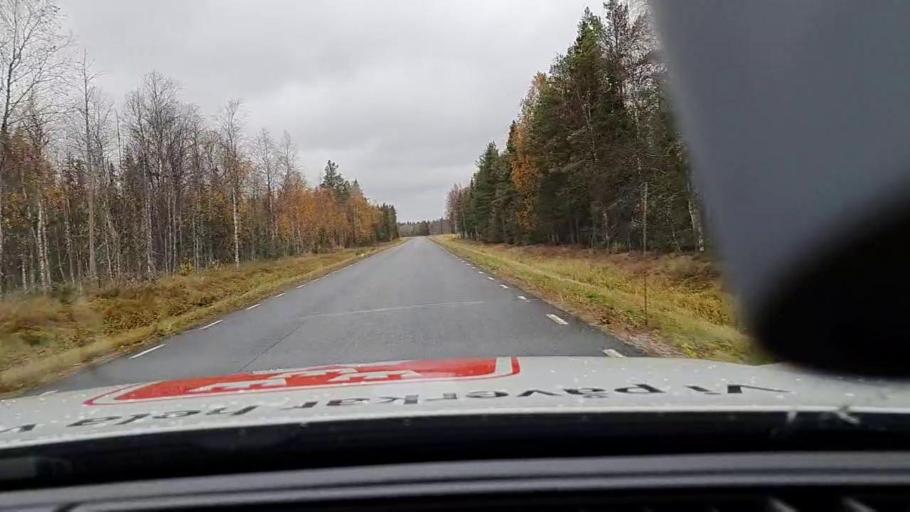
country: SE
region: Norrbotten
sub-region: Haparanda Kommun
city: Haparanda
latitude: 65.9290
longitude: 23.8176
